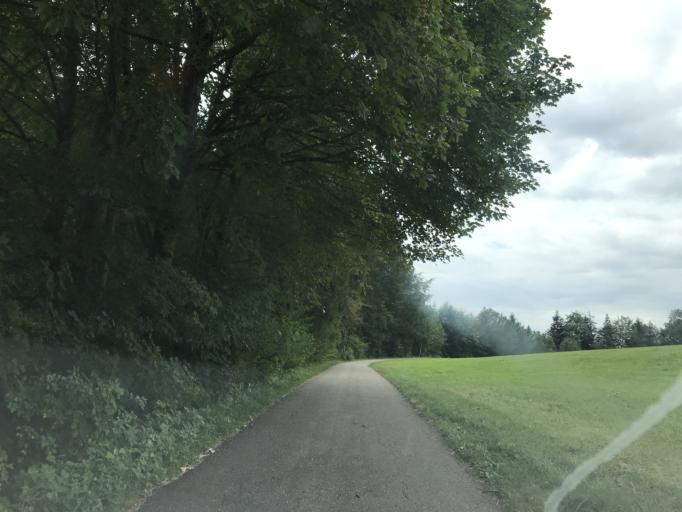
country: DE
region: Baden-Wuerttemberg
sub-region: Freiburg Region
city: Sankt Peter
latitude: 48.0072
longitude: 8.0274
